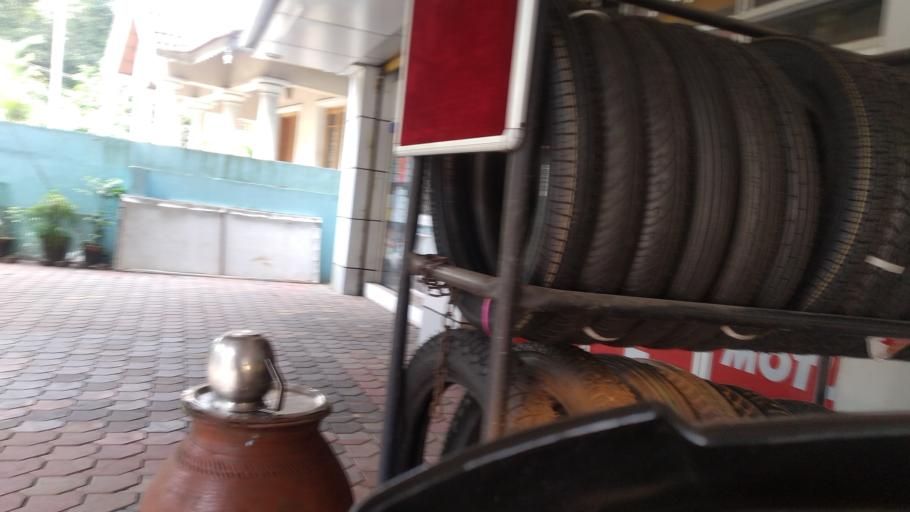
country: IN
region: Kerala
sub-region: Thrissur District
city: Kodungallur
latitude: 10.1408
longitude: 76.2312
